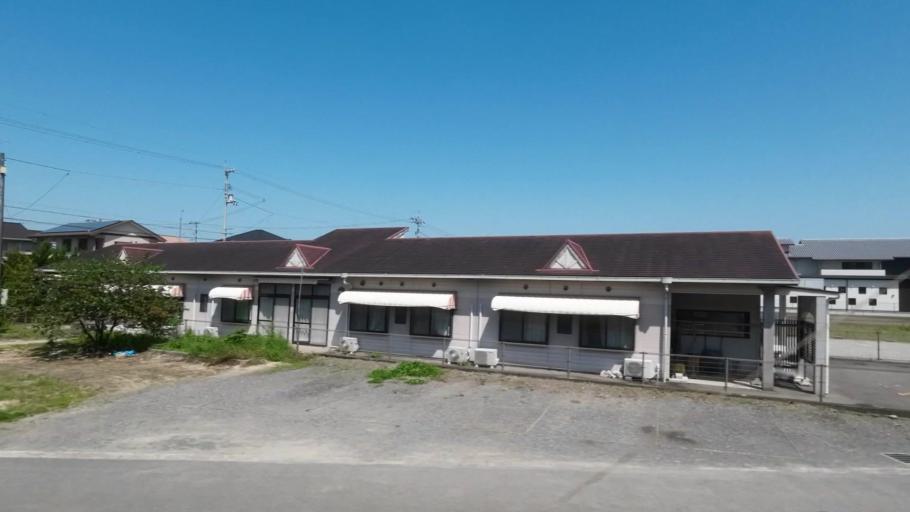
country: JP
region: Ehime
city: Niihama
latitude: 33.9610
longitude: 133.3099
